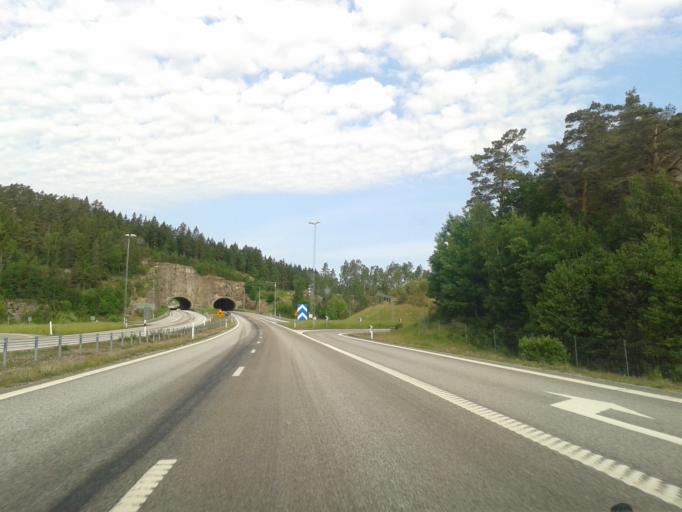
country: SE
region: Vaestra Goetaland
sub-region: Lysekils Kommun
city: Brastad
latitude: 58.5637
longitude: 11.4790
